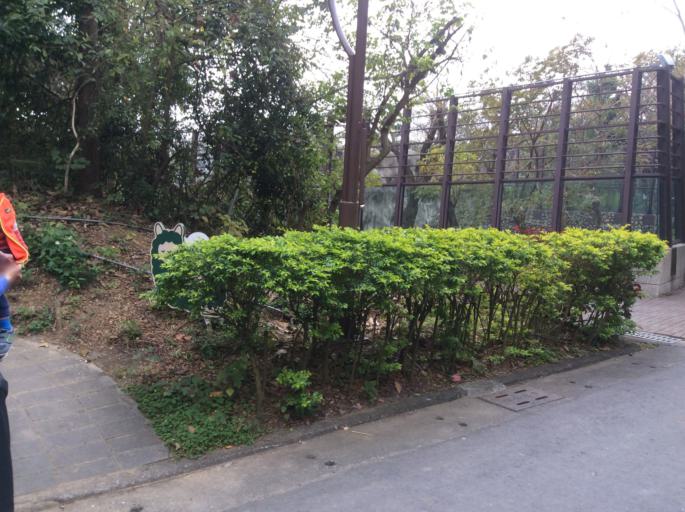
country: TW
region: Kaohsiung
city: Kaohsiung
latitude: 22.6369
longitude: 120.2754
